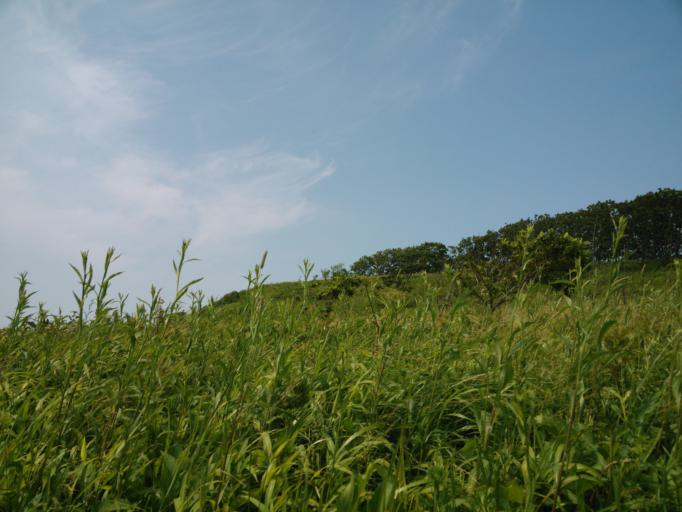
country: RU
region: Primorskiy
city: Vladivostok
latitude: 43.0941
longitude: 131.9881
